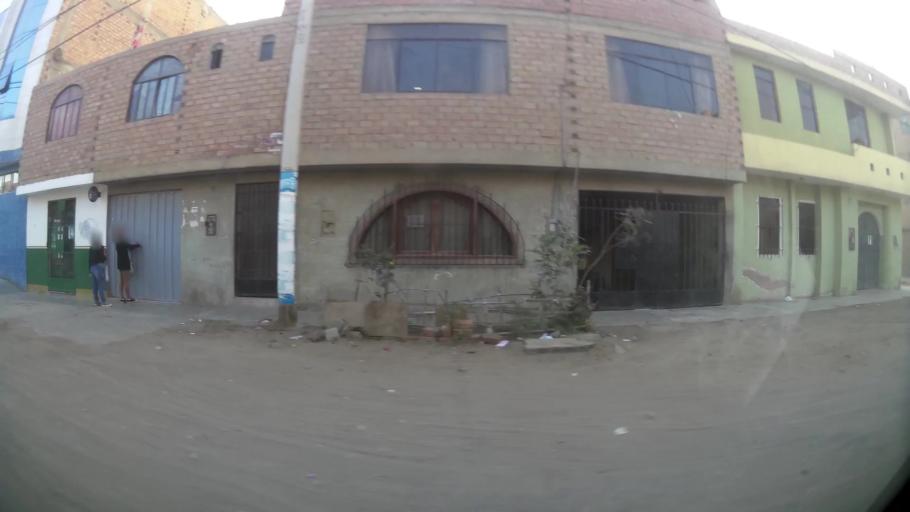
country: PE
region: Lima
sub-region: Huaura
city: Huacho
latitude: -11.1092
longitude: -77.6004
